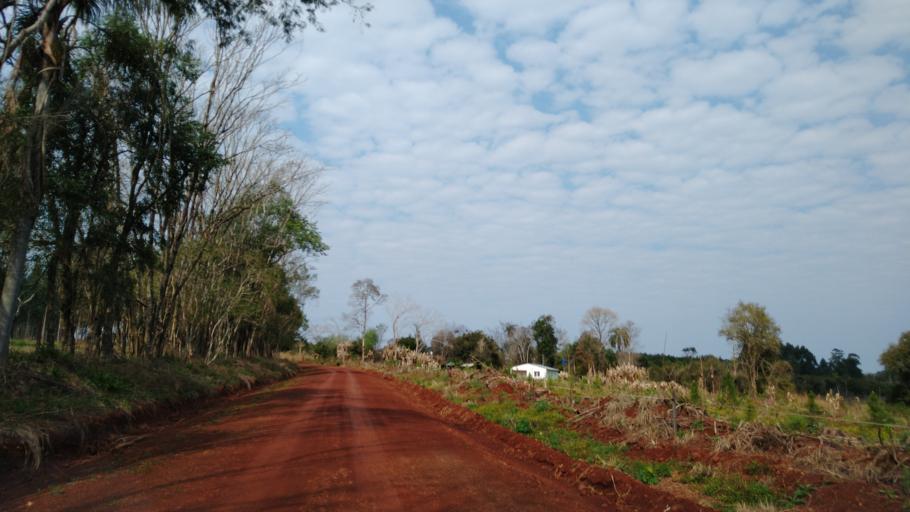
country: AR
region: Misiones
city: Capiovi
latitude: -26.9495
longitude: -55.0672
